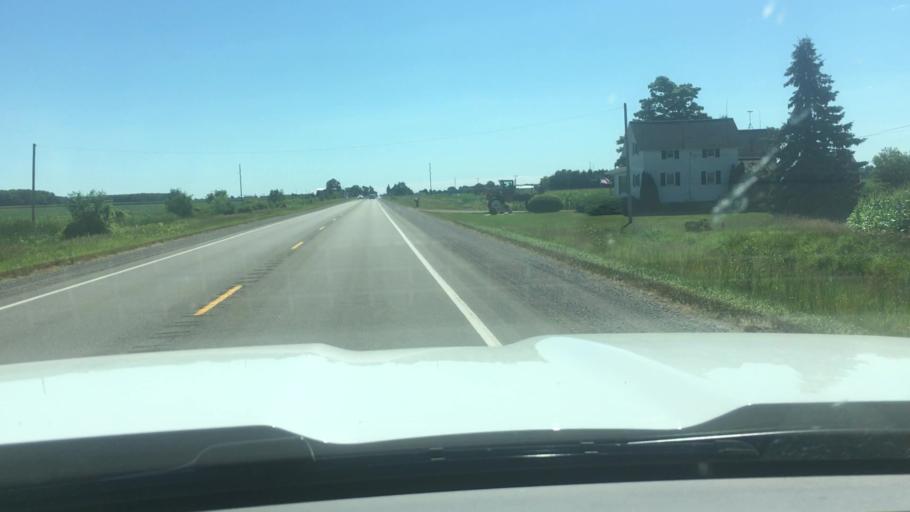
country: US
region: Michigan
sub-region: Montcalm County
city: Carson City
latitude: 43.1764
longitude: -84.7851
